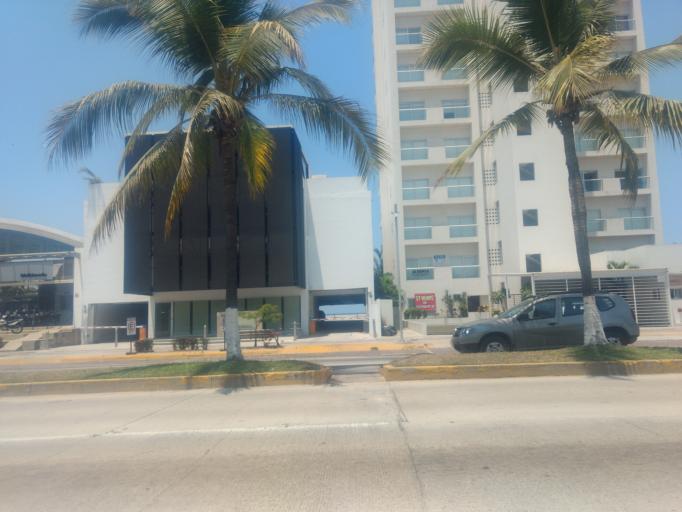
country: MX
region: Colima
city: Tapeixtles
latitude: 19.0879
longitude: -104.3113
